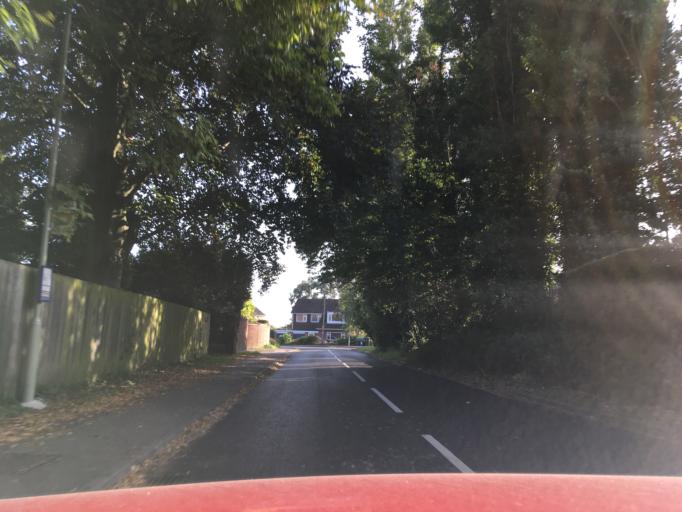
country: GB
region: England
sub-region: Gloucestershire
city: Gloucester
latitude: 51.8491
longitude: -2.2680
